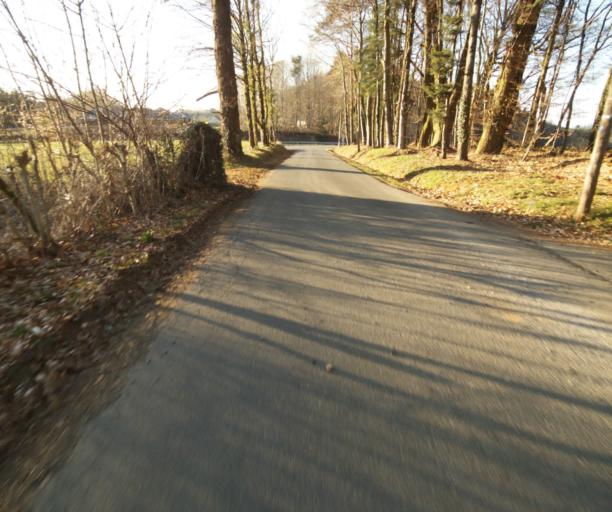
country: FR
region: Limousin
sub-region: Departement de la Correze
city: Seilhac
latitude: 45.3534
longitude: 1.7085
